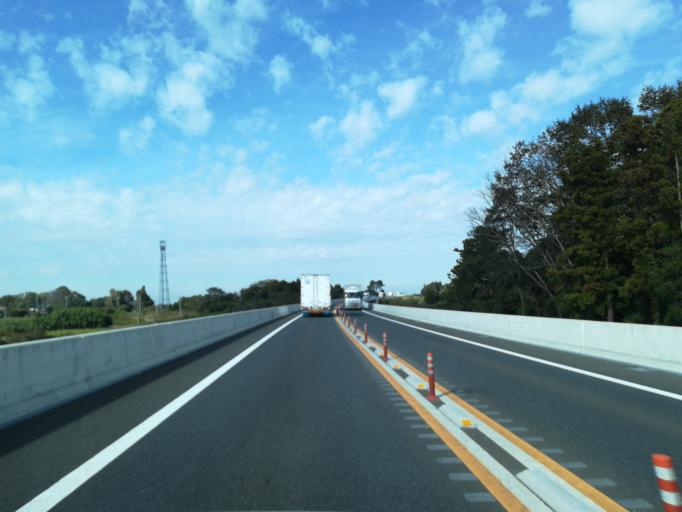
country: JP
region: Ibaraki
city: Mitsukaido
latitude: 36.0713
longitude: 140.0161
